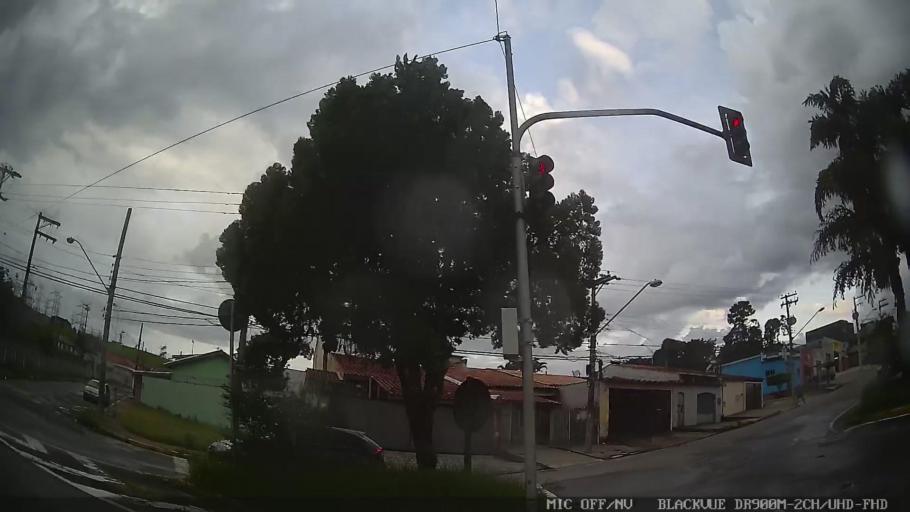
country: BR
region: Sao Paulo
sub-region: Mogi das Cruzes
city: Mogi das Cruzes
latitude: -23.5504
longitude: -46.1834
